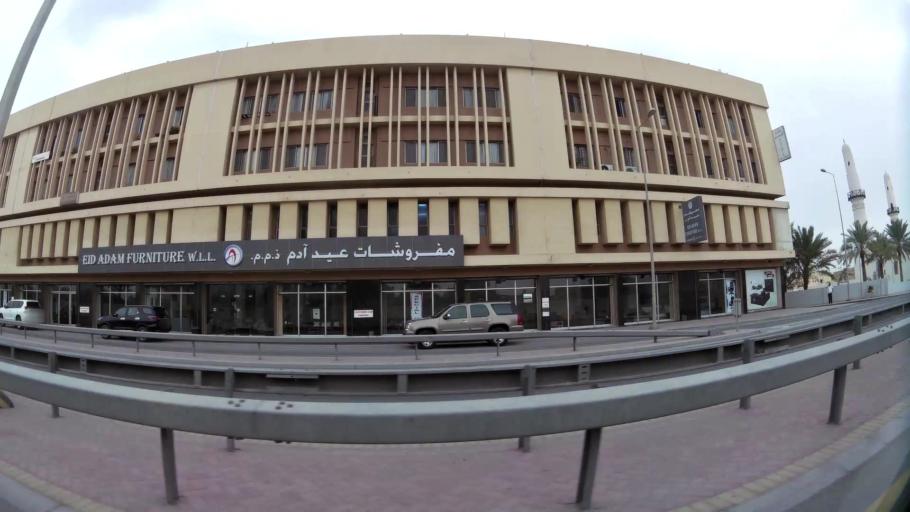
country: BH
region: Manama
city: Jidd Hafs
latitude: 26.2079
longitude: 50.5479
